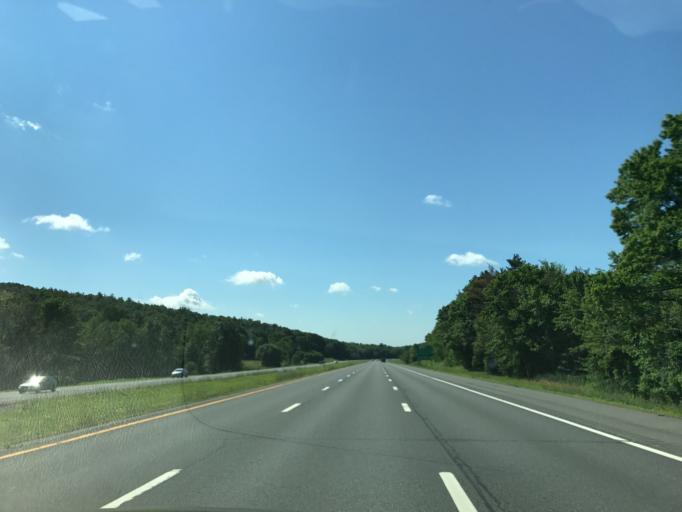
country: US
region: New York
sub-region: Rensselaer County
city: East Greenbush
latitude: 42.5984
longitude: -73.6807
